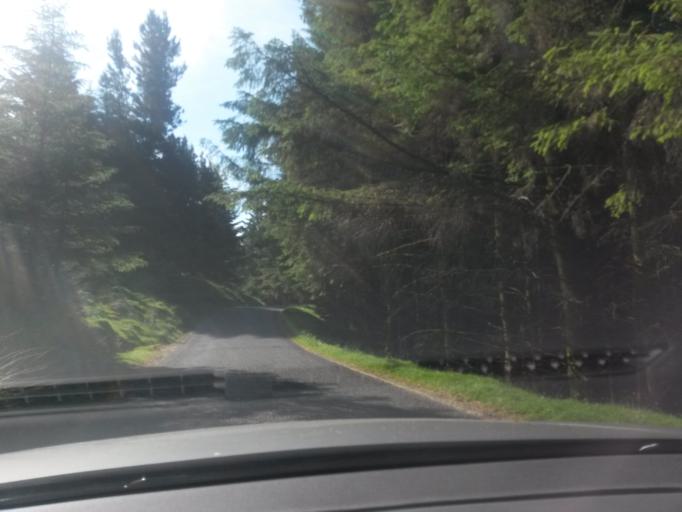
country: IE
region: Leinster
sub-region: Wicklow
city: Enniskerry
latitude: 53.1165
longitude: -6.2659
